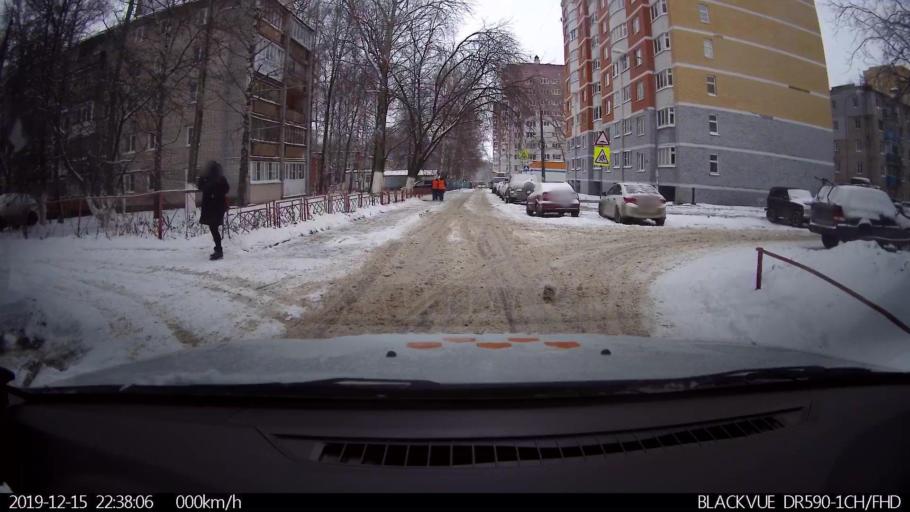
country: RU
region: Nizjnij Novgorod
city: Nizhniy Novgorod
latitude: 56.2390
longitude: 43.9705
